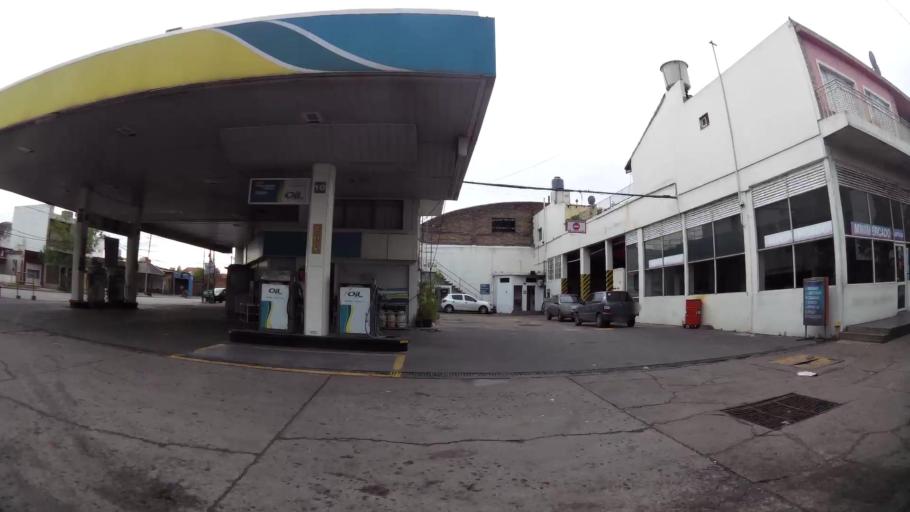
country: AR
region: Buenos Aires
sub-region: Partido de Lanus
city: Lanus
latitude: -34.7100
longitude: -58.3664
